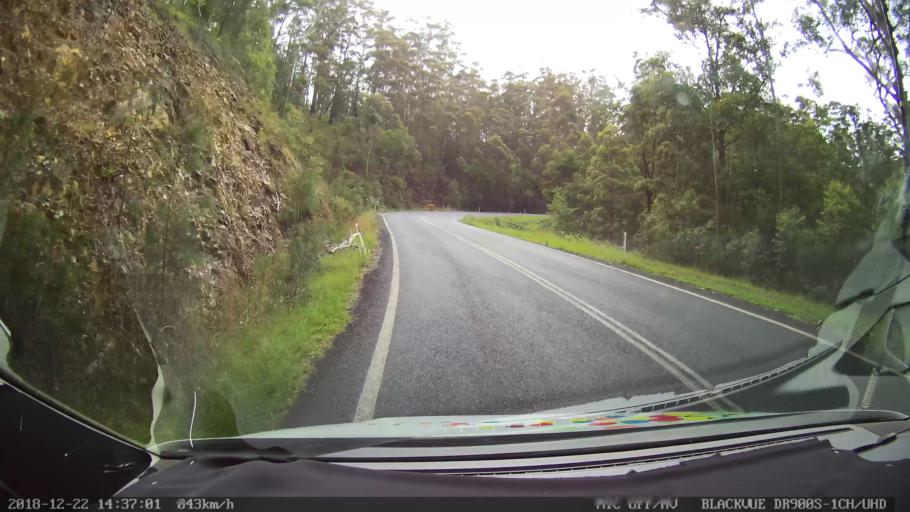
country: AU
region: New South Wales
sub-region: Bellingen
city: Dorrigo
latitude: -30.1317
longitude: 152.6032
